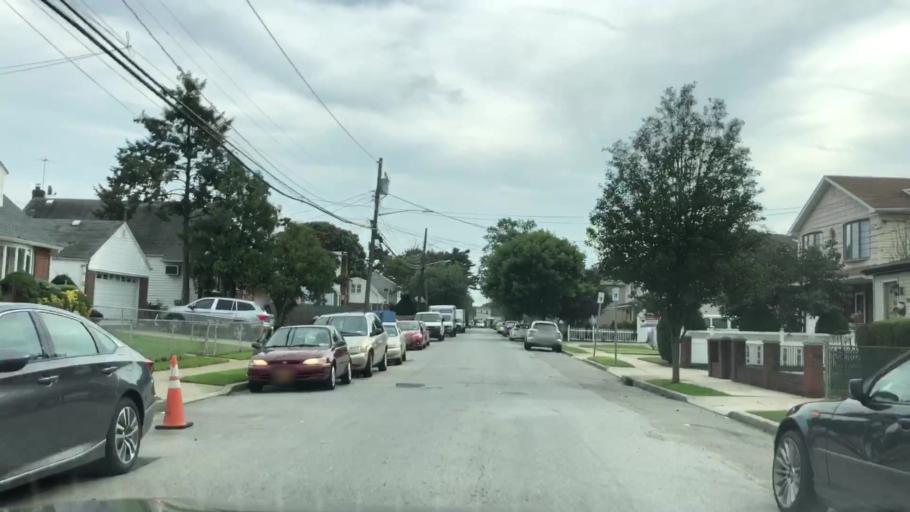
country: US
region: New York
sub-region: Nassau County
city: South Floral Park
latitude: 40.7033
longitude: -73.6913
